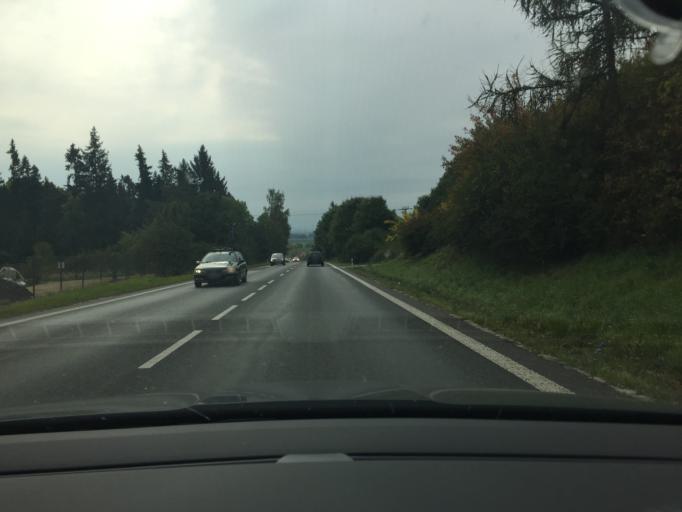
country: CZ
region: Jihocesky
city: Mirovice
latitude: 49.5462
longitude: 14.0817
